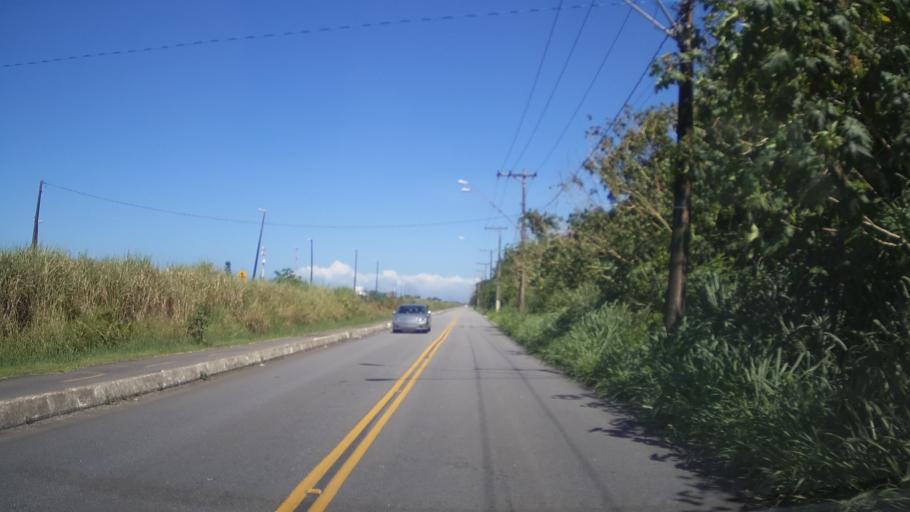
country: BR
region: Sao Paulo
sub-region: Mongagua
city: Mongagua
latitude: -24.0489
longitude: -46.5393
